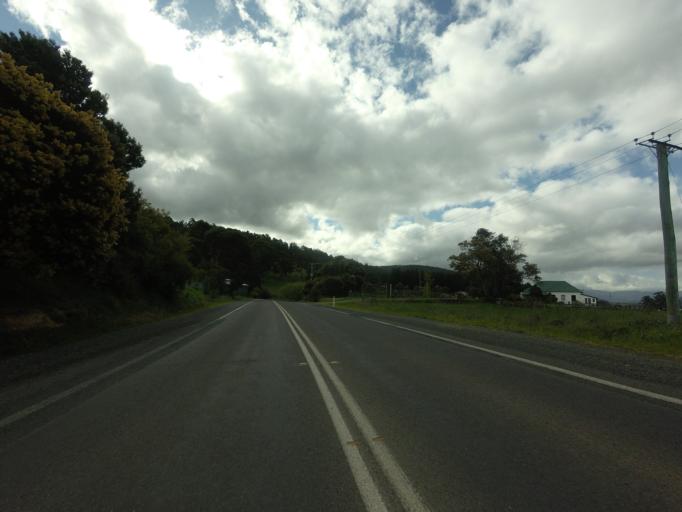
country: AU
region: Tasmania
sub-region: Huon Valley
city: Franklin
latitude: -43.1280
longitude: 146.9898
